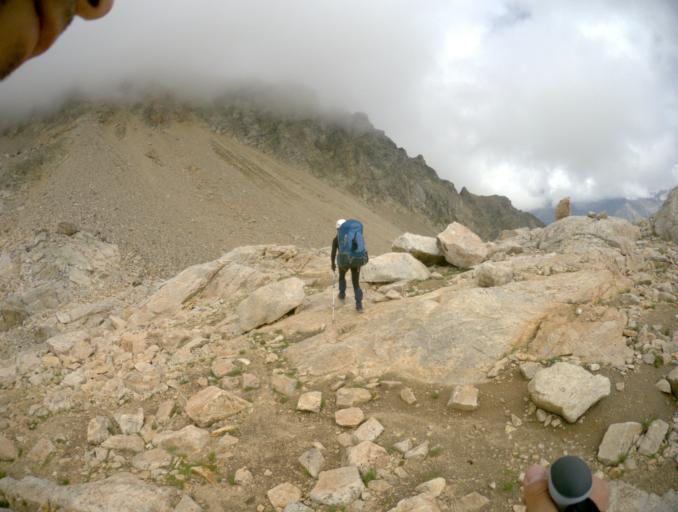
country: RU
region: Karachayevo-Cherkesiya
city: Uchkulan
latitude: 43.2764
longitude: 42.1178
